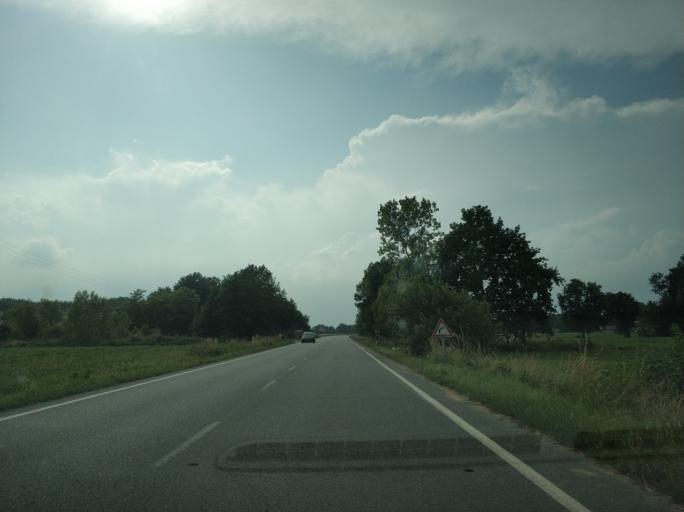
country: IT
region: Piedmont
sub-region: Provincia di Torino
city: Orio Canavese
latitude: 45.3120
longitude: 7.8417
